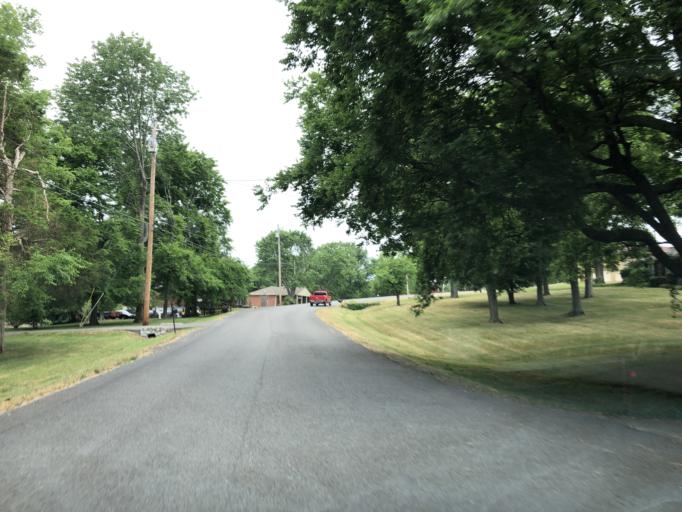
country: US
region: Tennessee
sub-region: Davidson County
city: Goodlettsville
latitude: 36.2819
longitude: -86.7383
